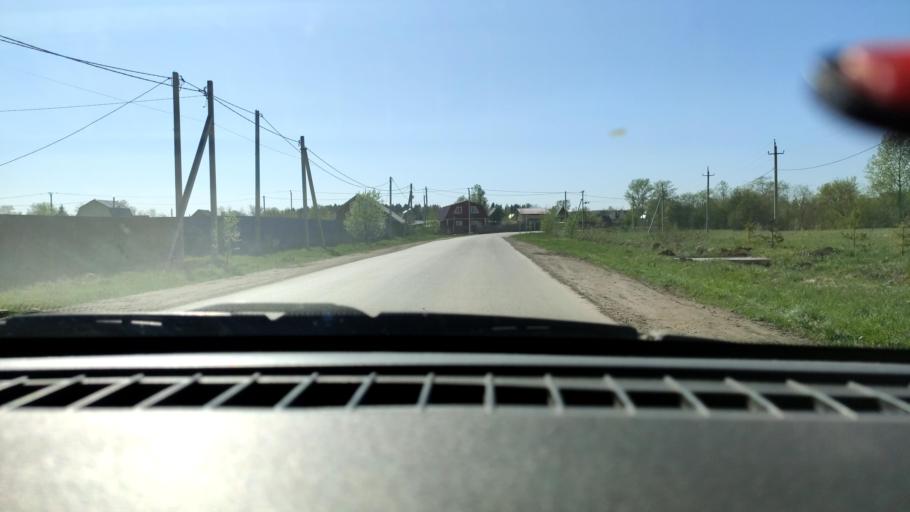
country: RU
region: Perm
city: Overyata
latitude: 58.0775
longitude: 55.9822
